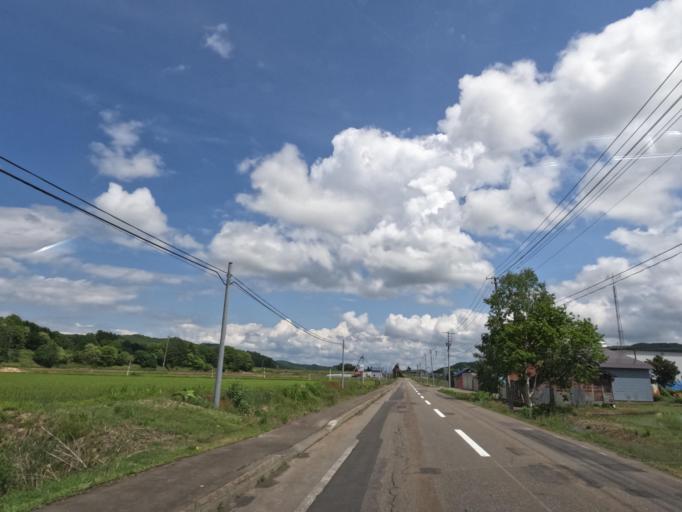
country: JP
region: Hokkaido
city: Takikawa
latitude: 43.5863
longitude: 141.7820
